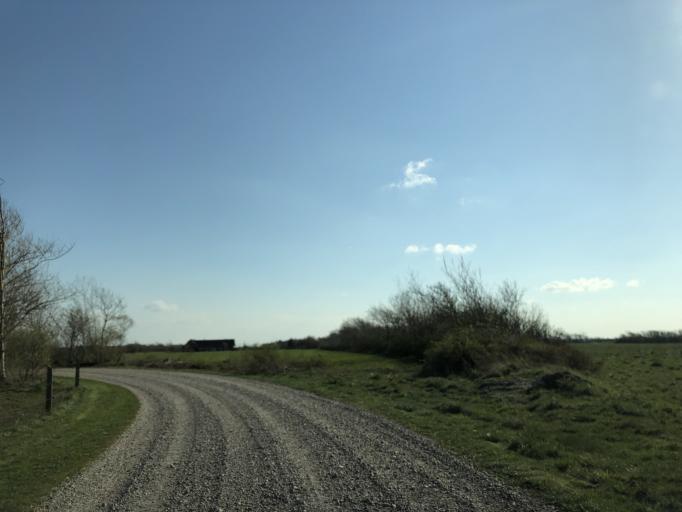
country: DK
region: Central Jutland
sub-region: Holstebro Kommune
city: Ulfborg
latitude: 56.3587
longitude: 8.2529
